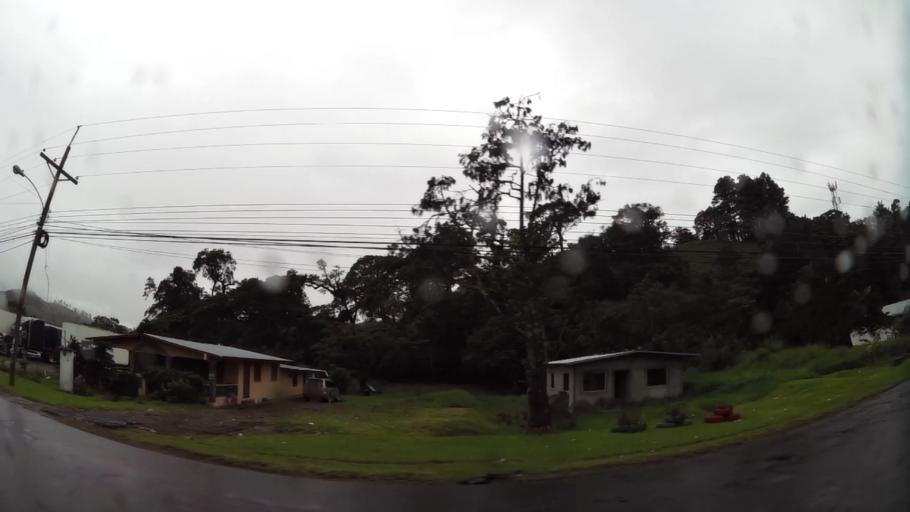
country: PA
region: Chiriqui
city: Volcan
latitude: 8.7740
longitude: -82.6382
